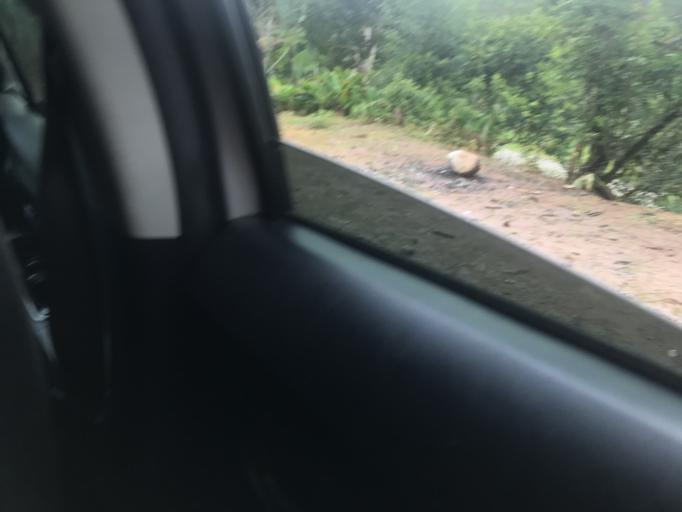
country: EC
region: Napo
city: Tena
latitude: -1.1239
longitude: -77.7986
